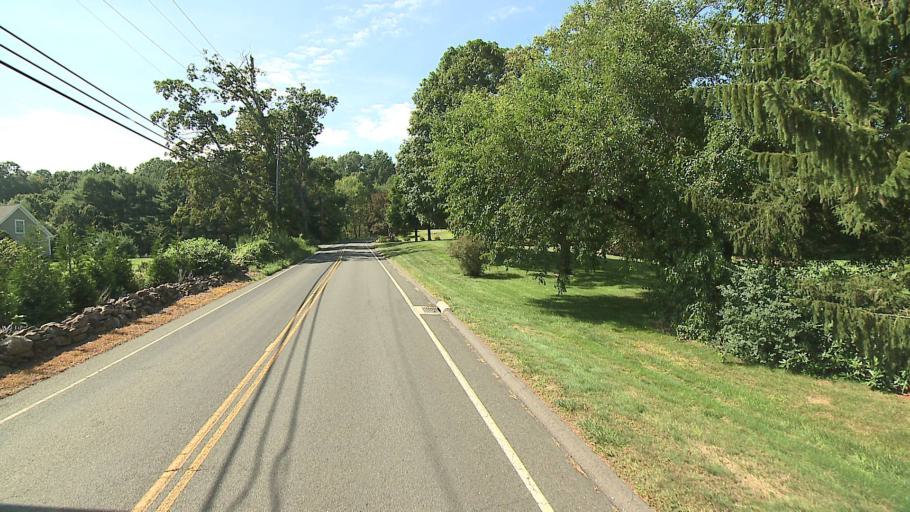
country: US
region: Connecticut
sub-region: Hartford County
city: West Simsbury
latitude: 41.8803
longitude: -72.8689
